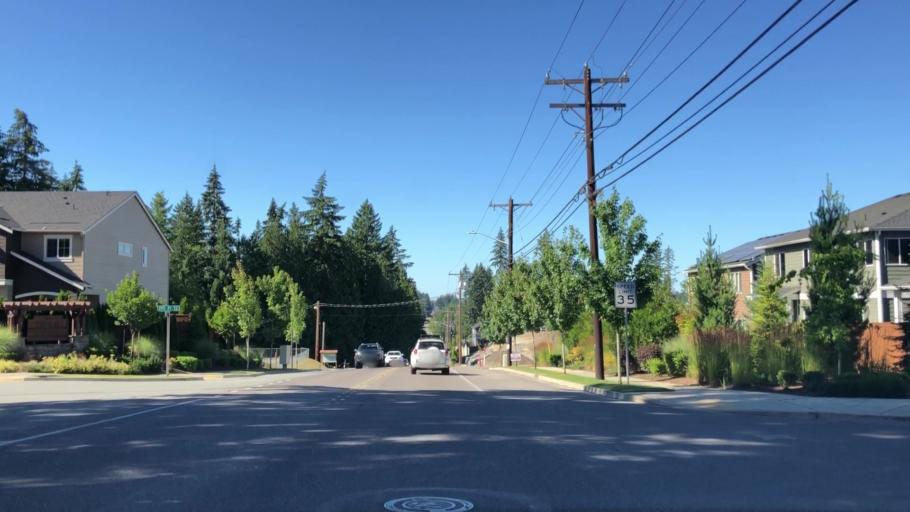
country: US
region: Washington
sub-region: Snohomish County
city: North Creek
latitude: 47.8202
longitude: -122.1860
